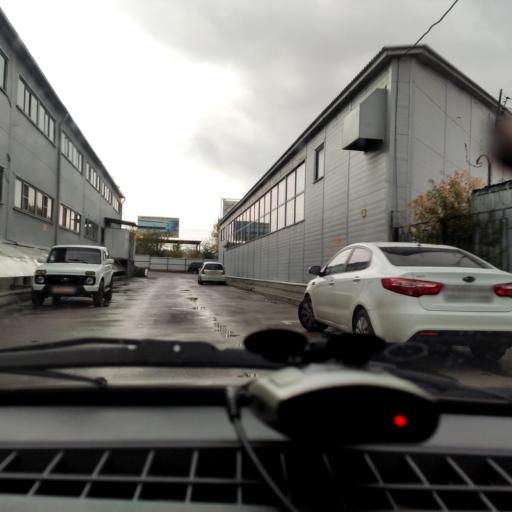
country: RU
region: Voronezj
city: Voronezh
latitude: 51.6692
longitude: 39.1296
